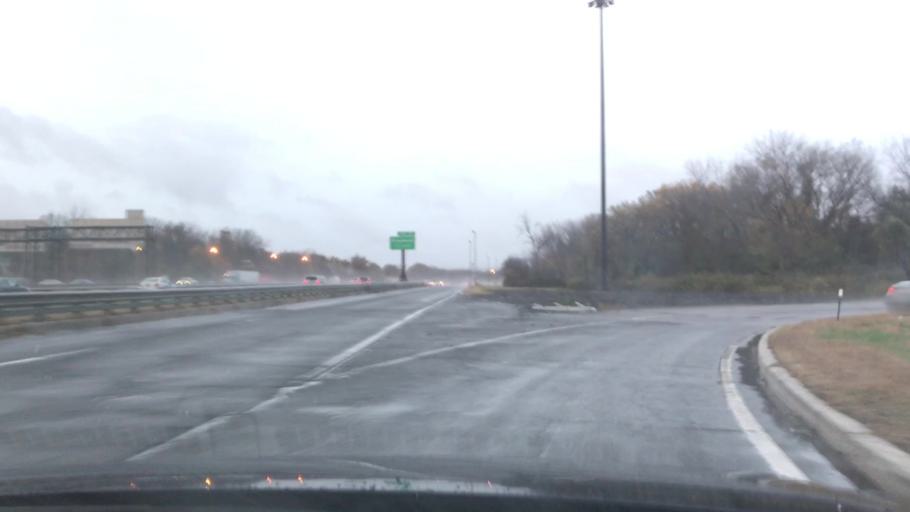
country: US
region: New Jersey
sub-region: Bergen County
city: Leonia
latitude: 40.8690
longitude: -74.0020
